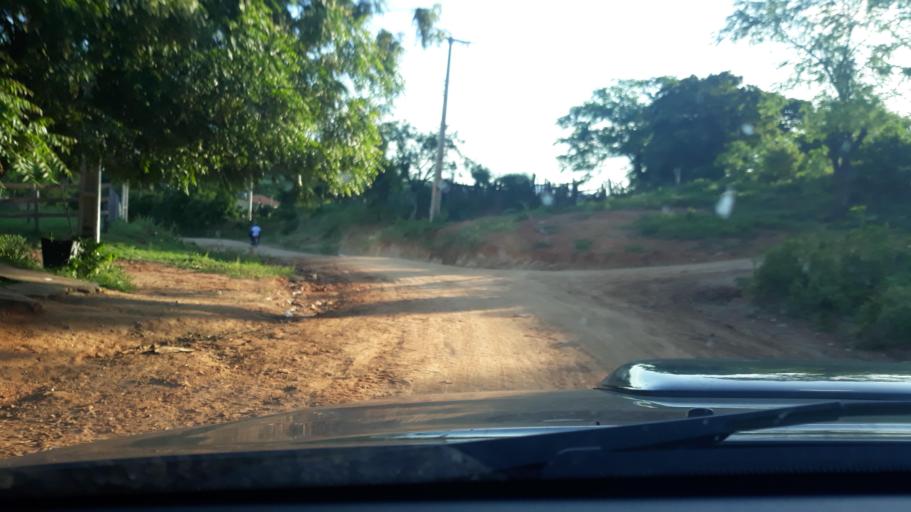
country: BR
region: Bahia
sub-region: Riacho De Santana
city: Riacho de Santana
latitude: -13.8262
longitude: -42.7273
